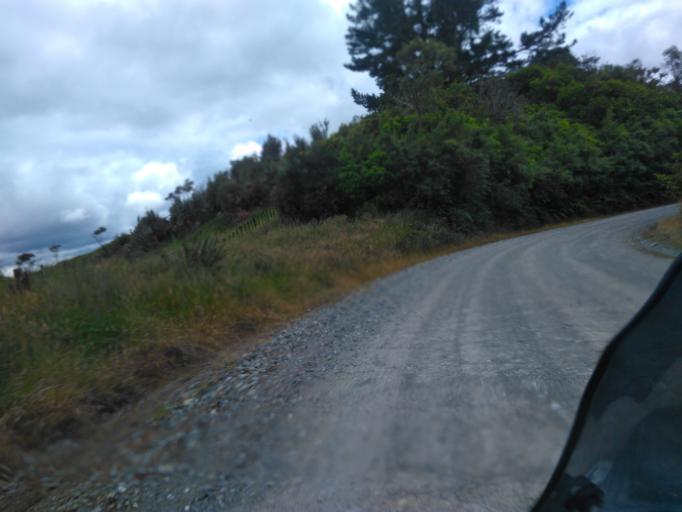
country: NZ
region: Gisborne
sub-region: Gisborne District
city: Gisborne
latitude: -38.1529
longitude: 178.1318
